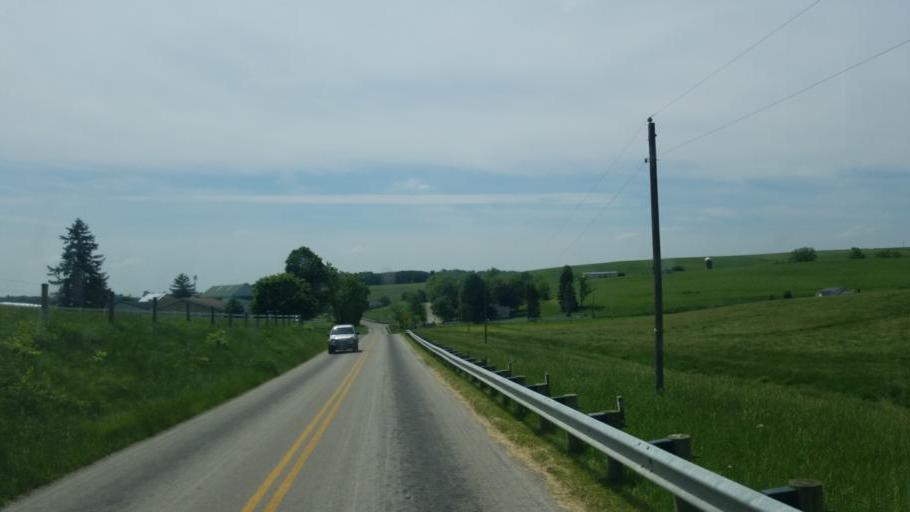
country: US
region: Ohio
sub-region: Tuscarawas County
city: Sugarcreek
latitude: 40.5126
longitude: -81.6860
